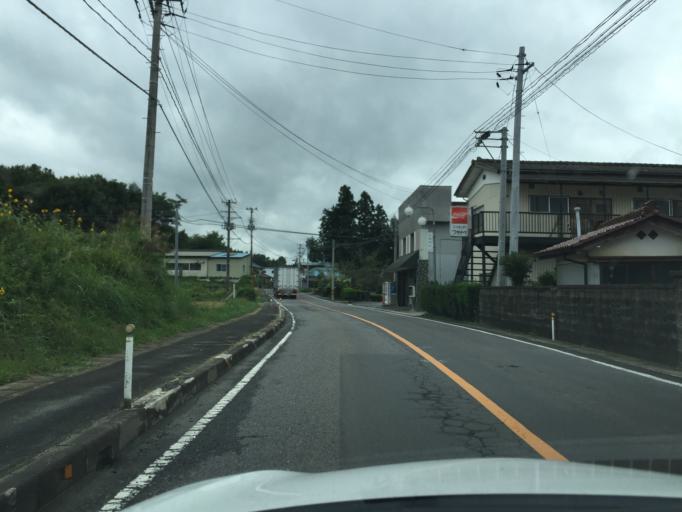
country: JP
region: Fukushima
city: Funehikimachi-funehiki
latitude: 37.4610
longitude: 140.5748
